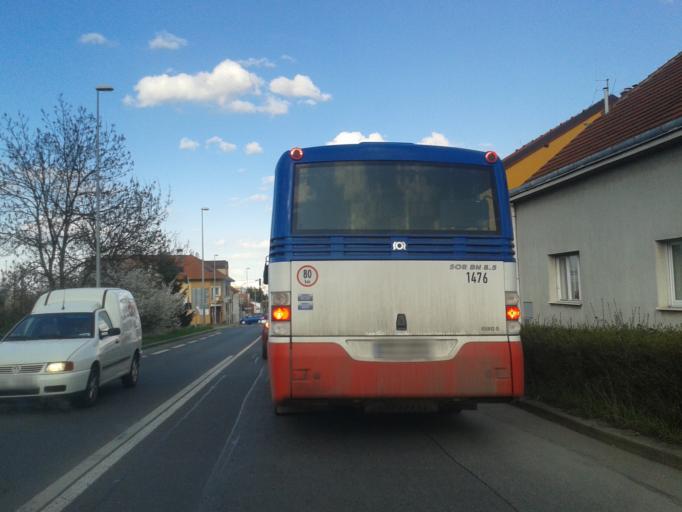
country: CZ
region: Central Bohemia
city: Hostivice
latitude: 50.0592
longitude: 14.2933
